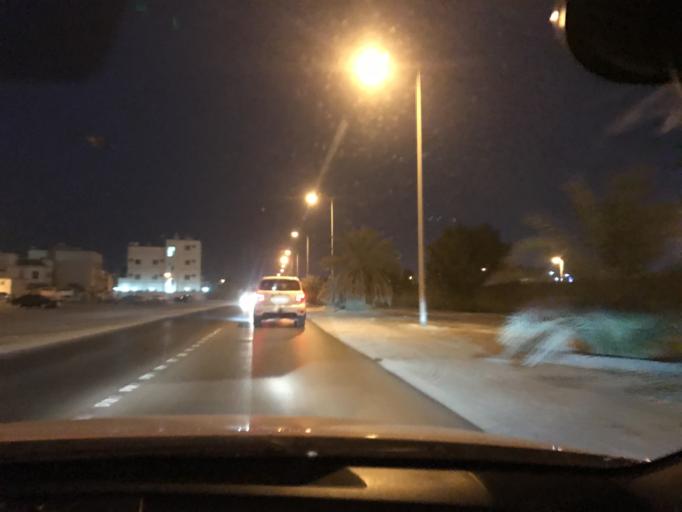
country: BH
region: Muharraq
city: Al Muharraq
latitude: 26.2808
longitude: 50.6234
